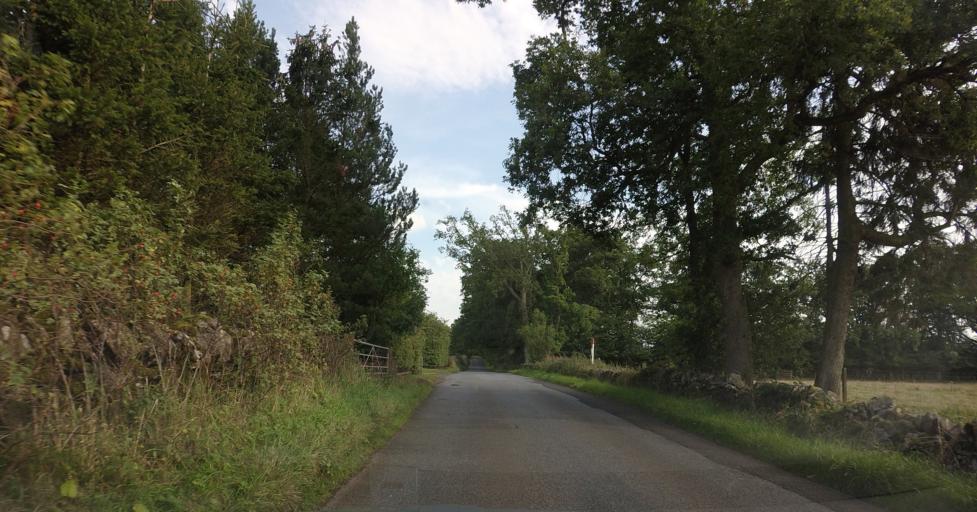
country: GB
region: Scotland
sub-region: Perth and Kinross
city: Auchterarder
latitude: 56.3055
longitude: -3.7270
